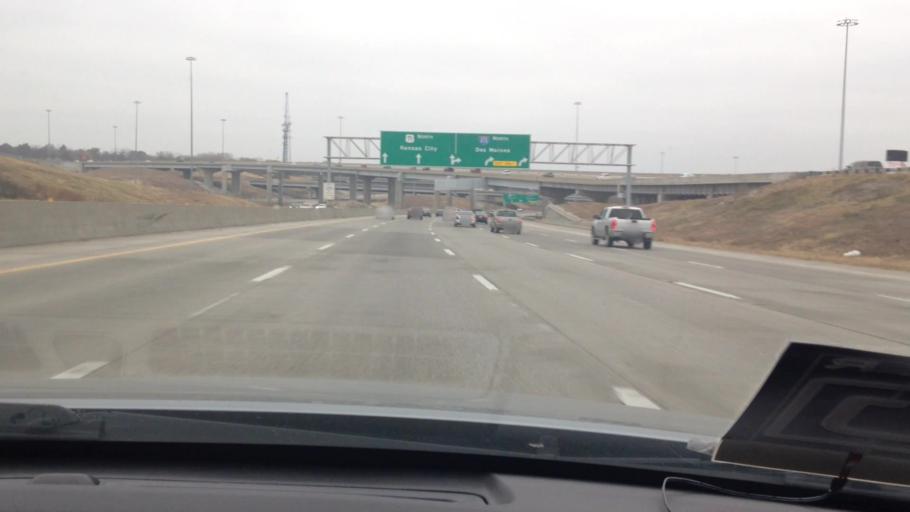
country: US
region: Missouri
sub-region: Jackson County
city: Grandview
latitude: 38.9360
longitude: -94.5325
